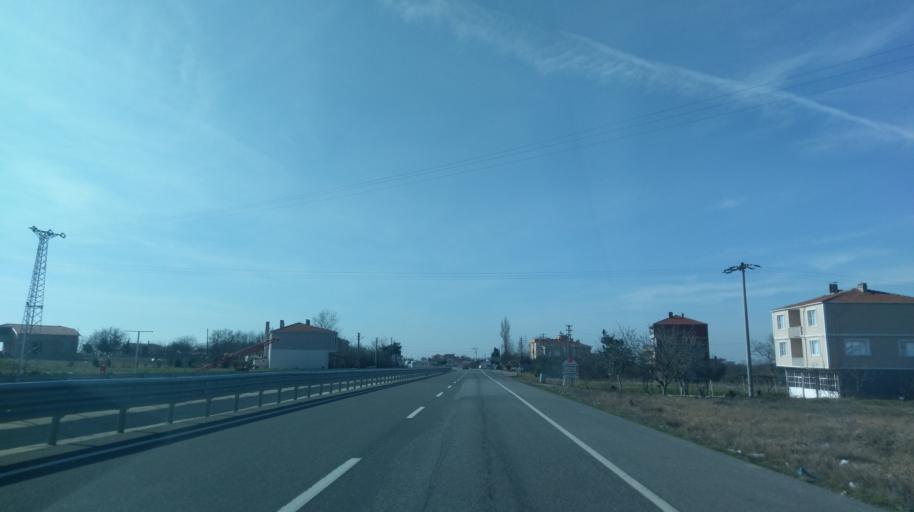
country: TR
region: Edirne
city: Hamidiye
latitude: 41.1557
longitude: 26.6646
